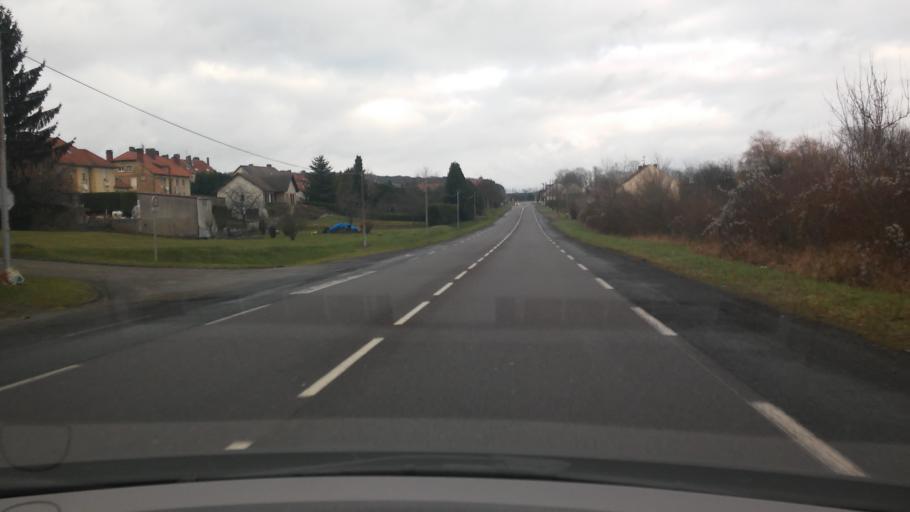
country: FR
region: Lorraine
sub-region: Departement de la Moselle
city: Longeville-les-Saint-Avold
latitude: 49.1201
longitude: 6.5846
